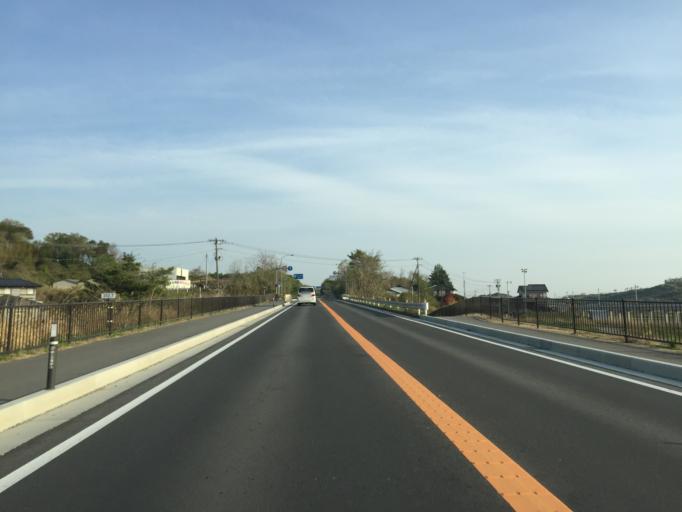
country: JP
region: Miyagi
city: Watari
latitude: 37.9267
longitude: 140.8983
